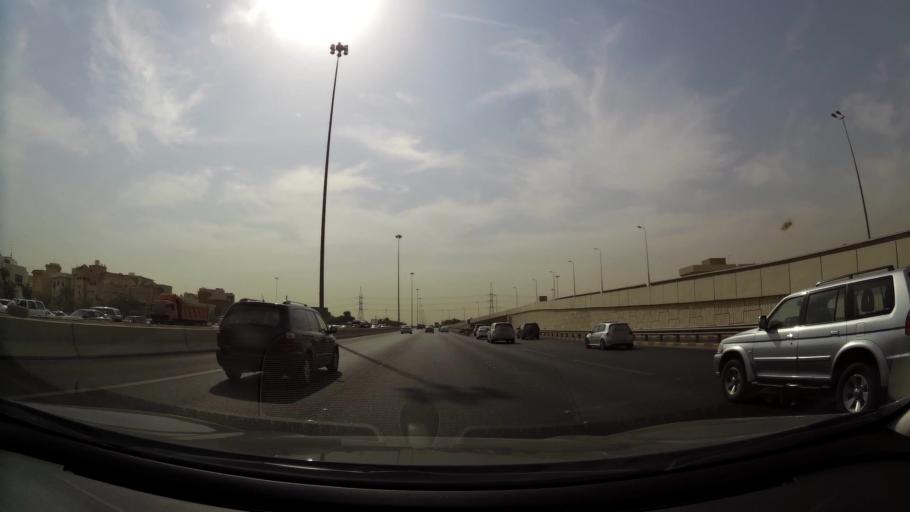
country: KW
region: Al Farwaniyah
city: Al Farwaniyah
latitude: 29.3085
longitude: 47.9776
